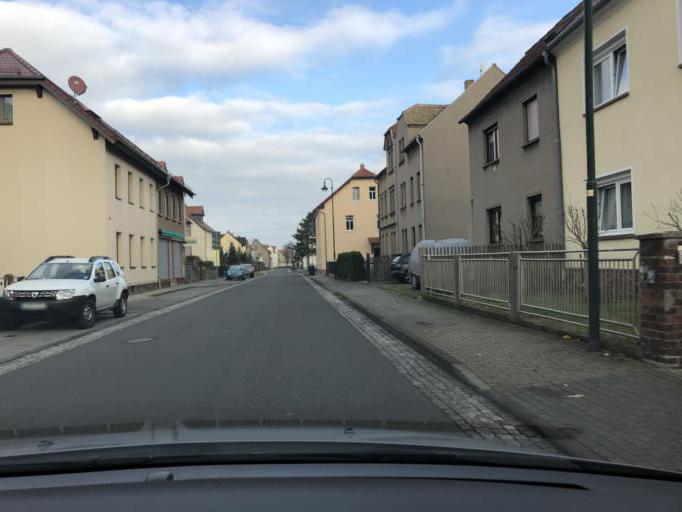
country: DE
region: Saxony
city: Nerchau
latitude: 51.2745
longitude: 12.7927
